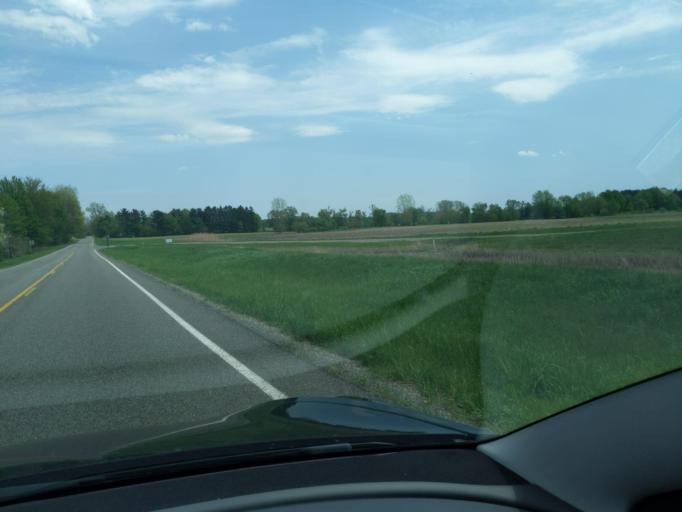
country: US
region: Michigan
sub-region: Ingham County
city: Stockbridge
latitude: 42.4899
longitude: -84.2913
